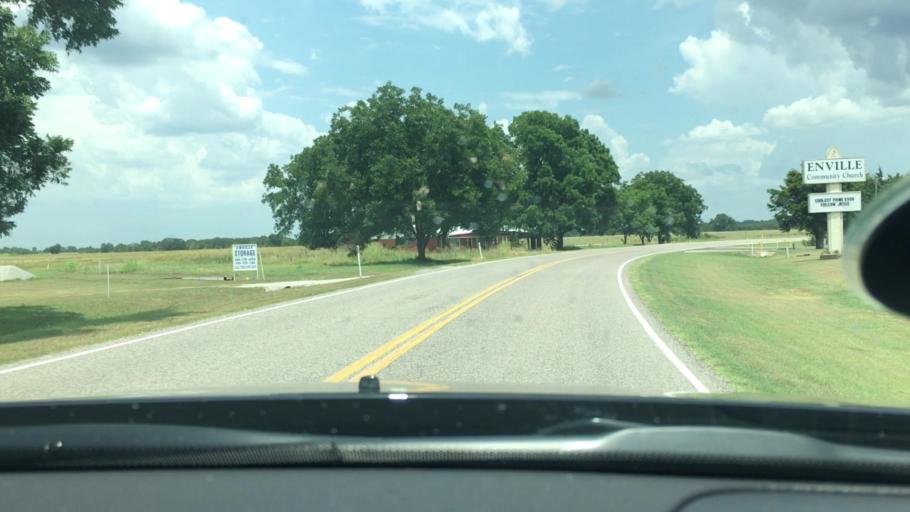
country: US
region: Oklahoma
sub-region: Love County
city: Marietta
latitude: 33.9827
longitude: -96.9864
